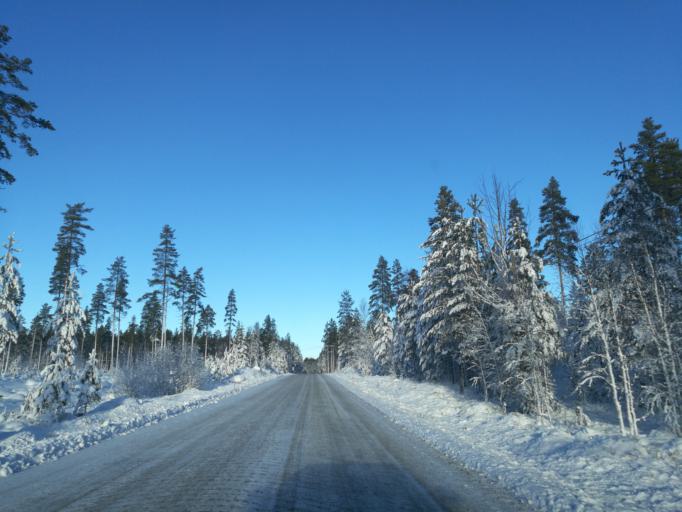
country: NO
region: Hedmark
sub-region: Grue
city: Kirkenaer
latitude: 60.5040
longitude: 12.5586
